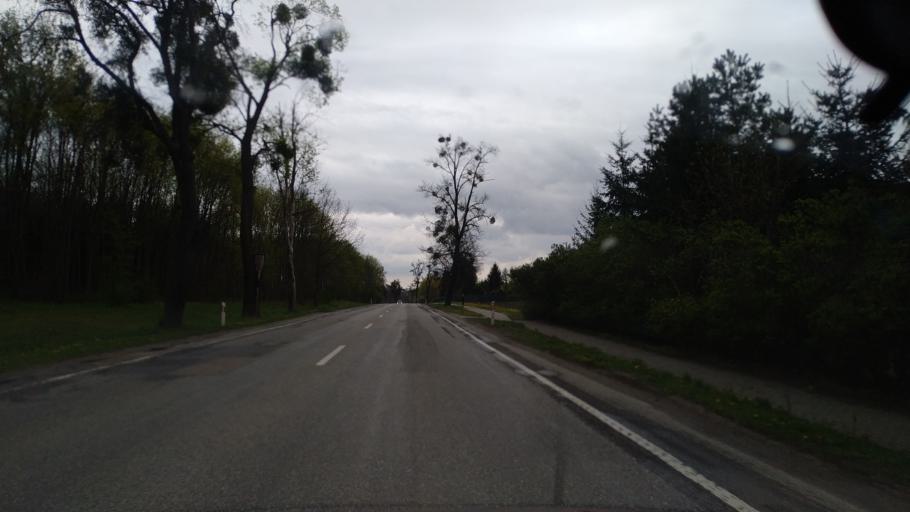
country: PL
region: Pomeranian Voivodeship
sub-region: Powiat tczewski
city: Pelplin
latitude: 54.0303
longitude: 18.6488
